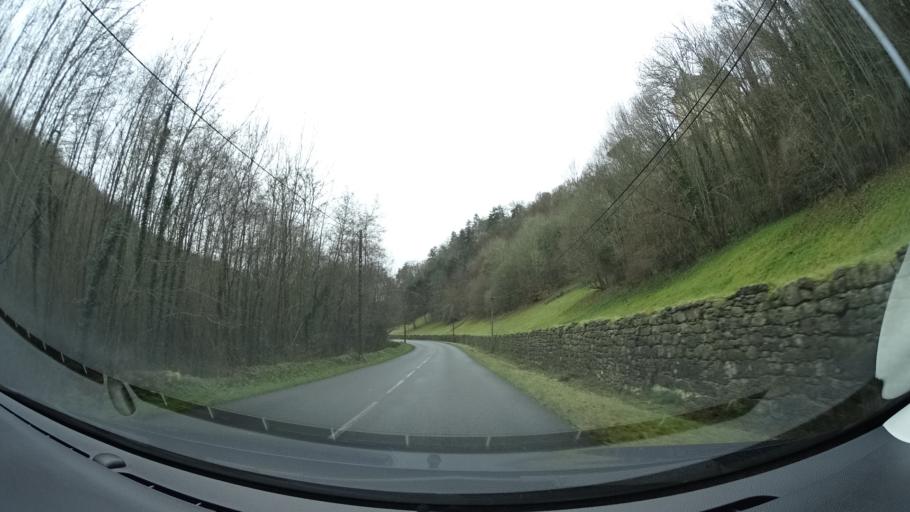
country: FR
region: Aquitaine
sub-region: Departement de la Dordogne
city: Saint-Cyprien
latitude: 44.8833
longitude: 1.0659
